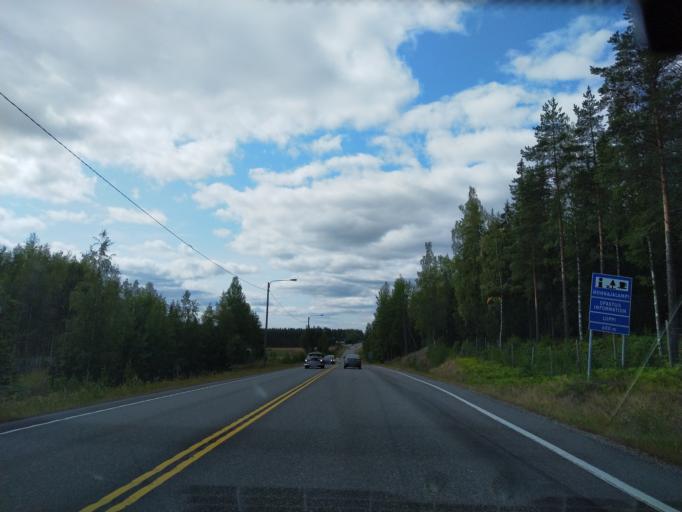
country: FI
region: Haeme
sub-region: Riihimaeki
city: Loppi
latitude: 60.7310
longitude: 24.5307
